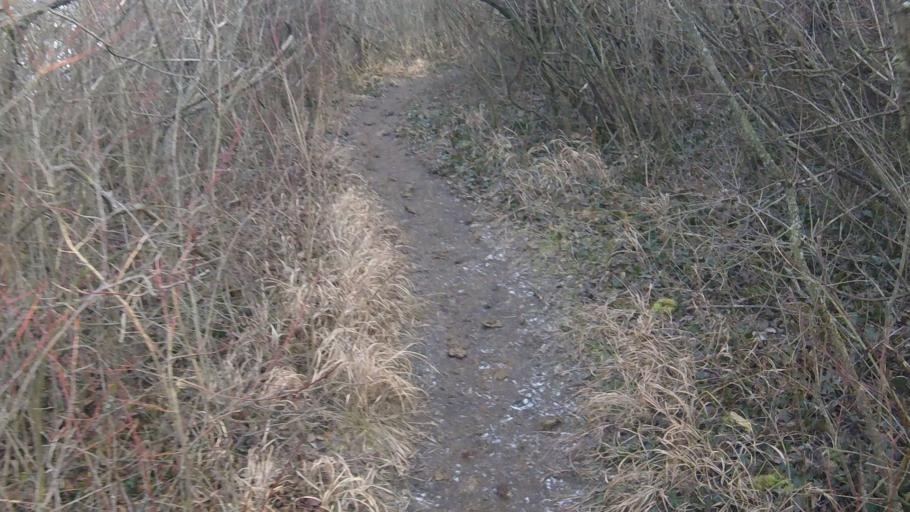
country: HU
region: Pest
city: Urom
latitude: 47.5972
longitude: 19.0318
